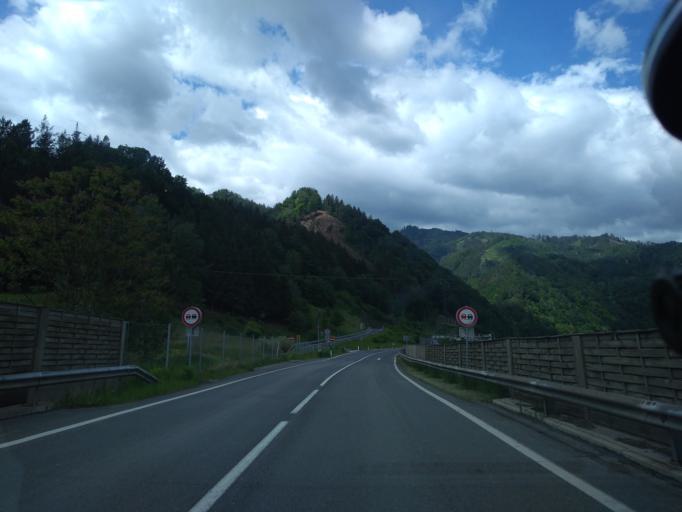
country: AT
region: Styria
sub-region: Politischer Bezirk Bruck-Muerzzuschlag
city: Pernegg an der Mur
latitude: 47.3695
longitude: 15.3178
